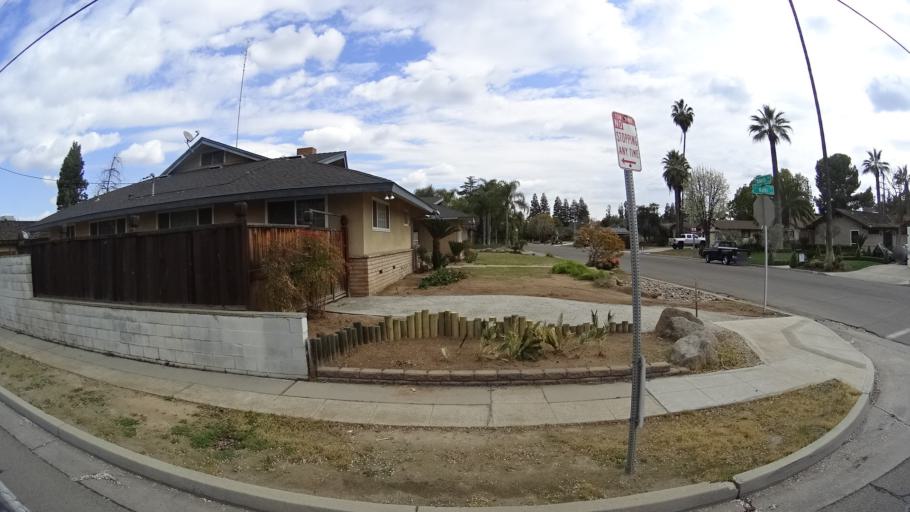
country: US
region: California
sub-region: Fresno County
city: Fresno
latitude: 36.8201
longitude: -119.8444
